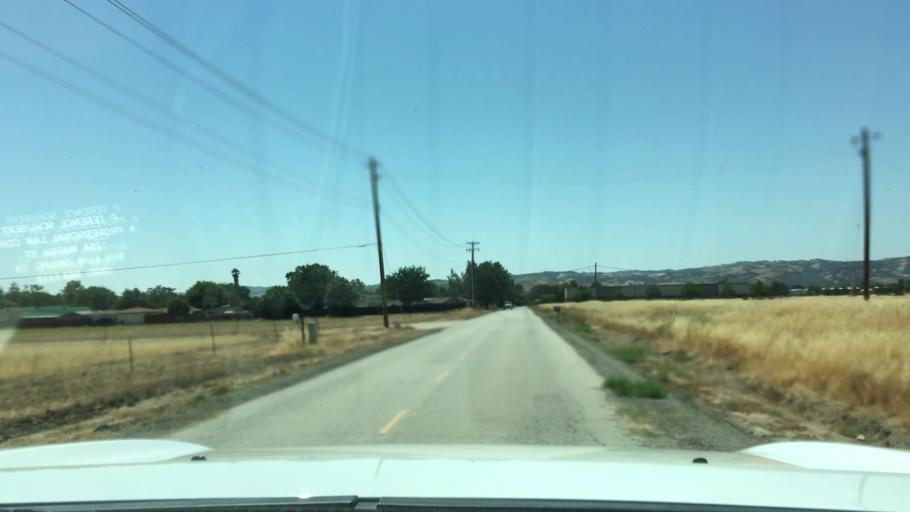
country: US
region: California
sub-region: San Luis Obispo County
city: Paso Robles
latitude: 35.6119
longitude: -120.6393
